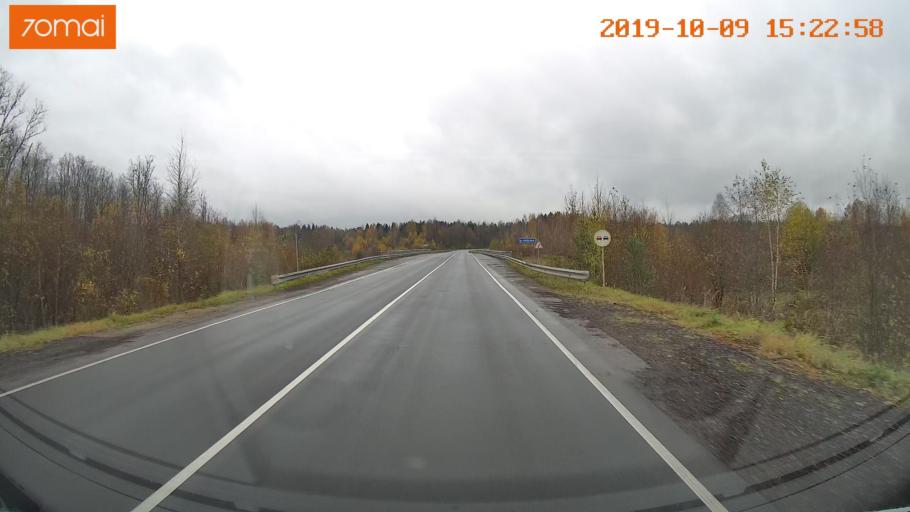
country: RU
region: Kostroma
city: Susanino
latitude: 58.0398
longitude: 41.4884
